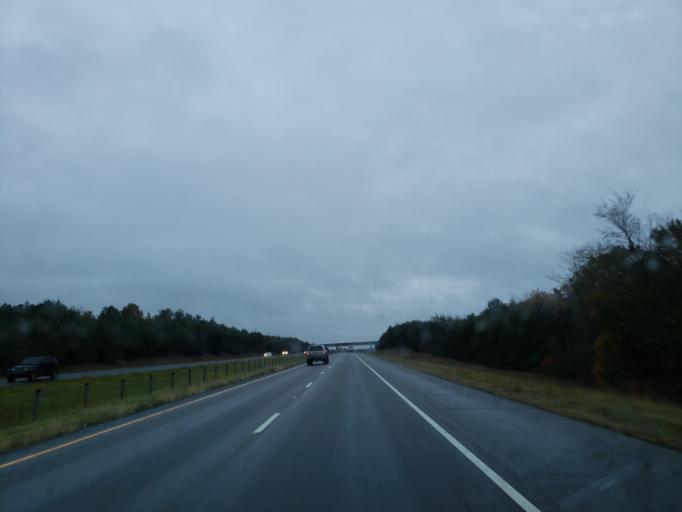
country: US
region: Alabama
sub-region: Sumter County
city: Livingston
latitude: 32.6772
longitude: -88.1668
